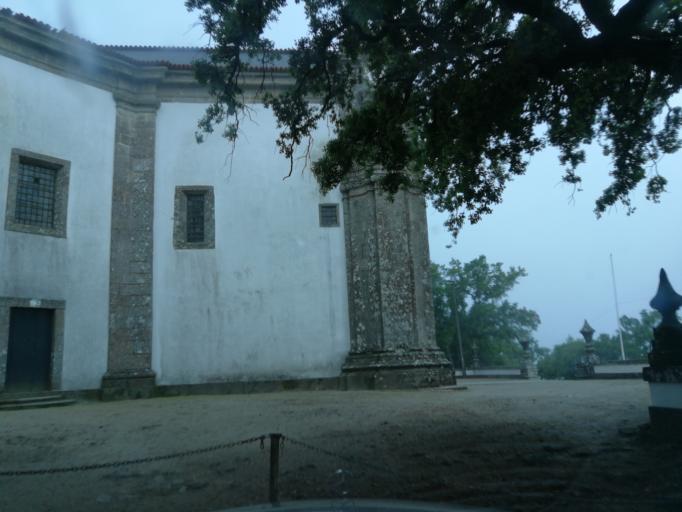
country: PT
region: Braga
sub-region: Braga
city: Braga
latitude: 41.5222
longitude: -8.3876
